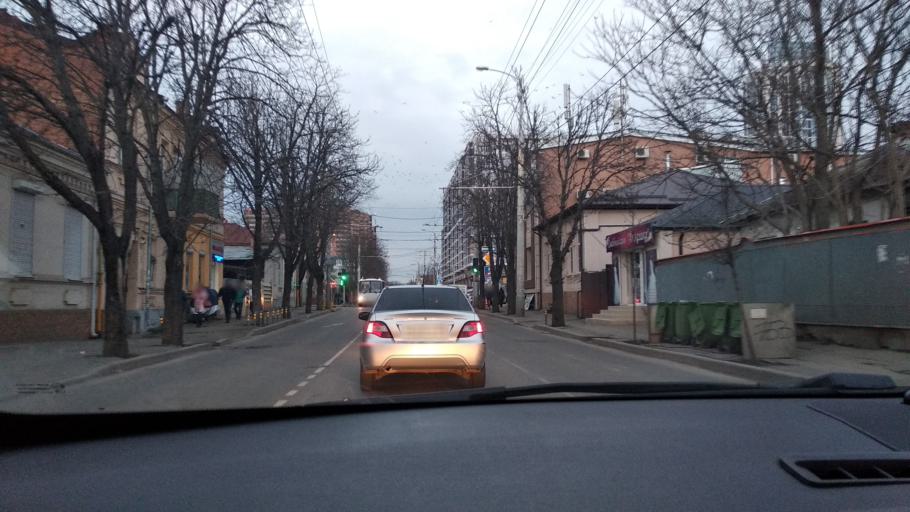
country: RU
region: Krasnodarskiy
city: Krasnodar
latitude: 45.0341
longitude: 38.9692
